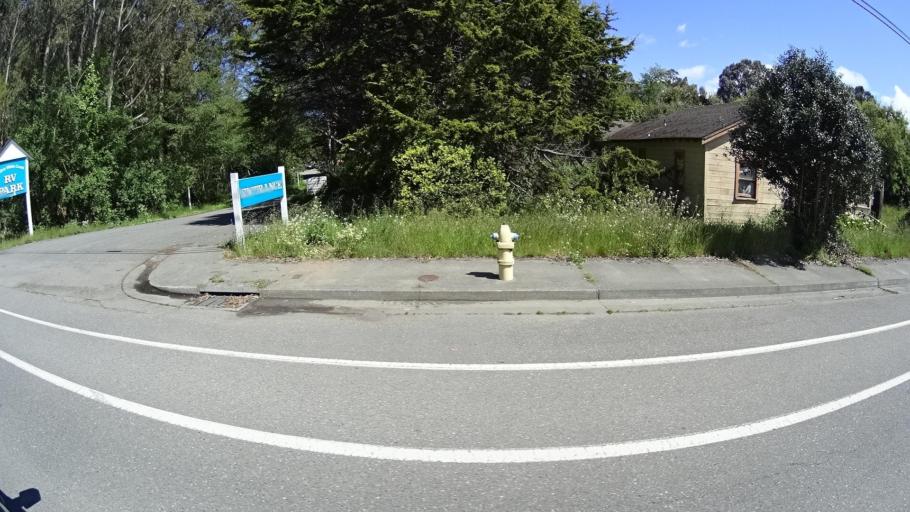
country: US
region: California
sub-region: Humboldt County
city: McKinleyville
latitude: 40.9563
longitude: -124.1136
